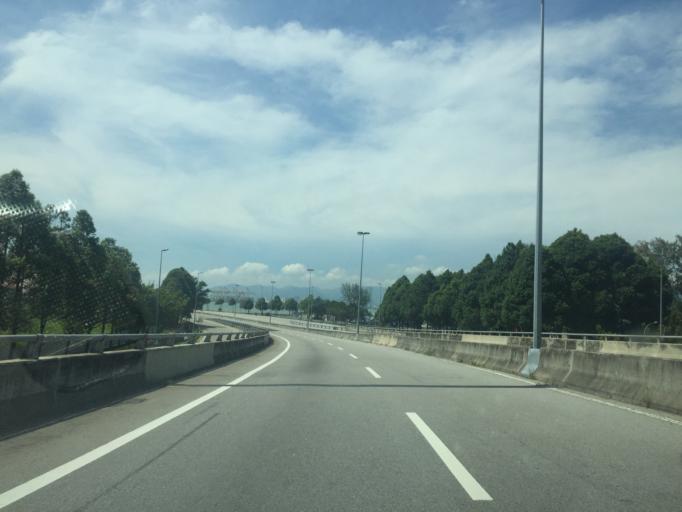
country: MY
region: Penang
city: Permatang Kuching
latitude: 5.4421
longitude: 100.3807
